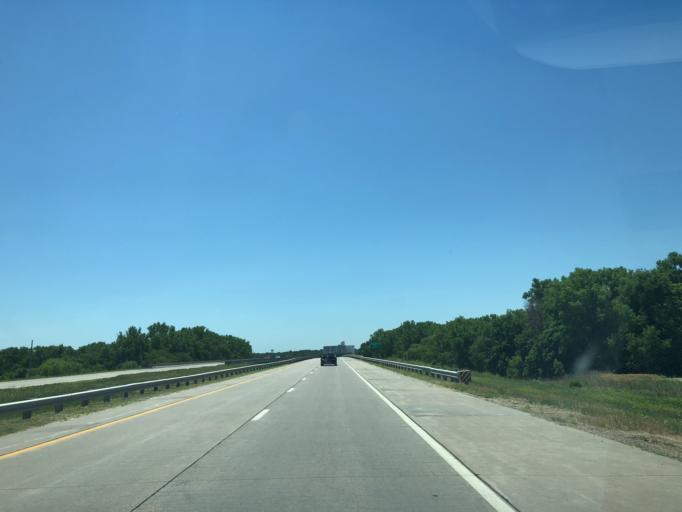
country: US
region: Kansas
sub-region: Cloud County
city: Concordia
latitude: 39.5927
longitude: -97.6593
